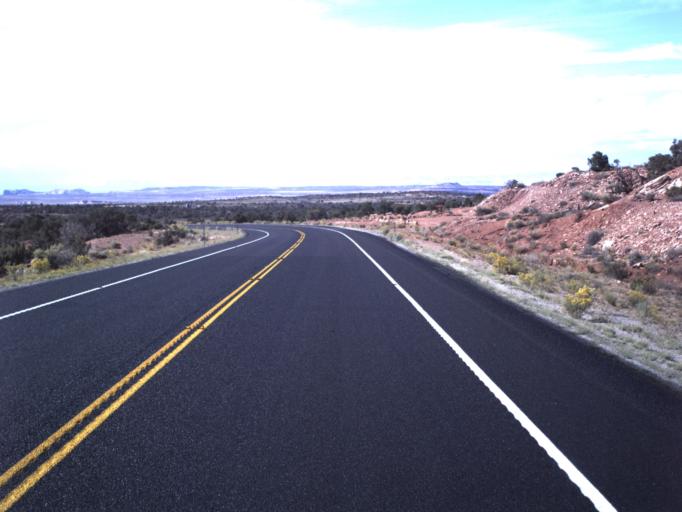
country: US
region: Utah
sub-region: Grand County
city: Moab
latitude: 38.5796
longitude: -109.7970
